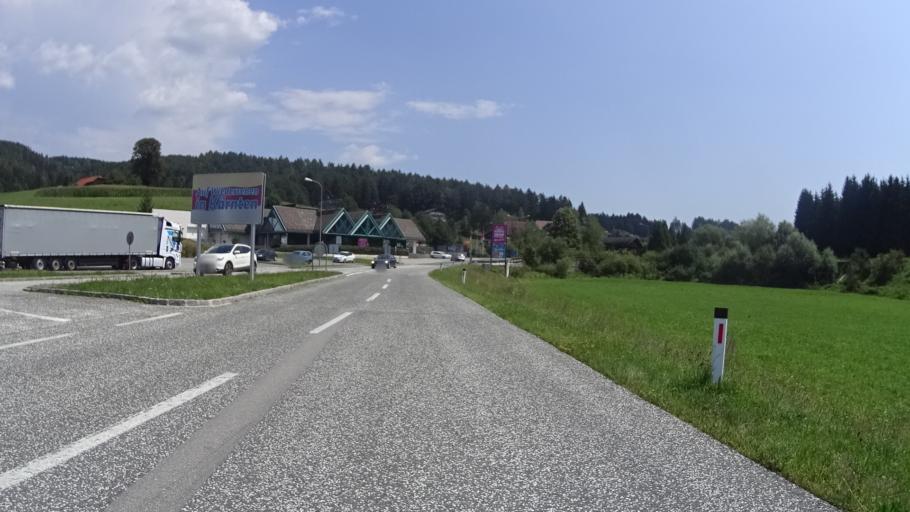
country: AT
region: Carinthia
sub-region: Politischer Bezirk Volkermarkt
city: Bleiburg/Pliberk
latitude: 46.5675
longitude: 14.8379
